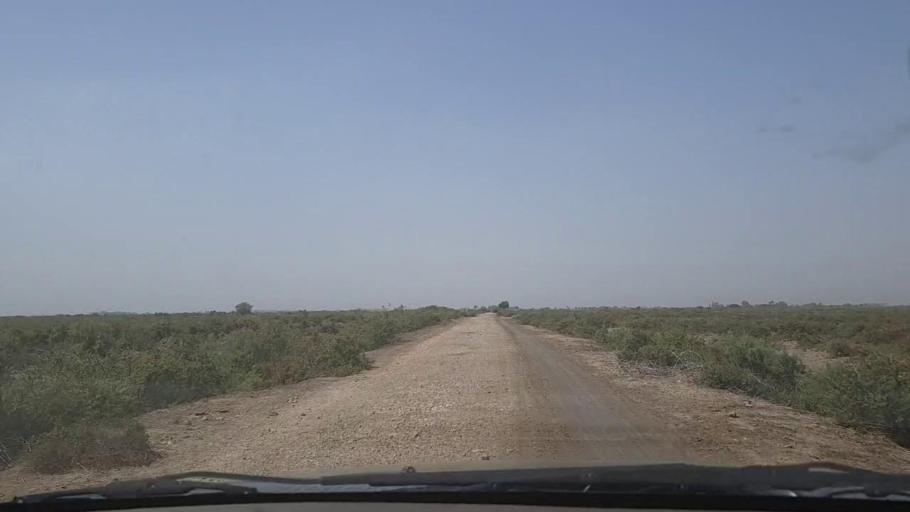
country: PK
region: Sindh
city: Keti Bandar
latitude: 24.2611
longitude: 67.6599
